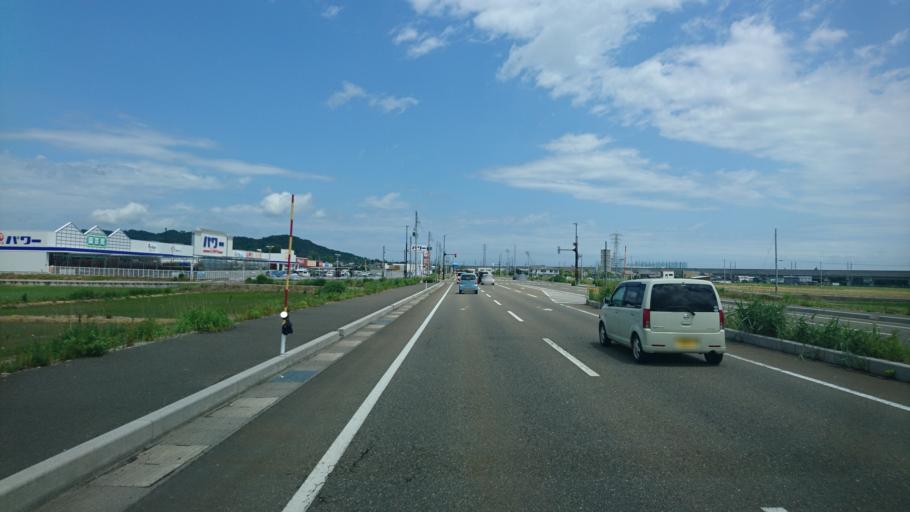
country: JP
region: Niigata
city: Joetsu
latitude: 37.0876
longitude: 138.2335
